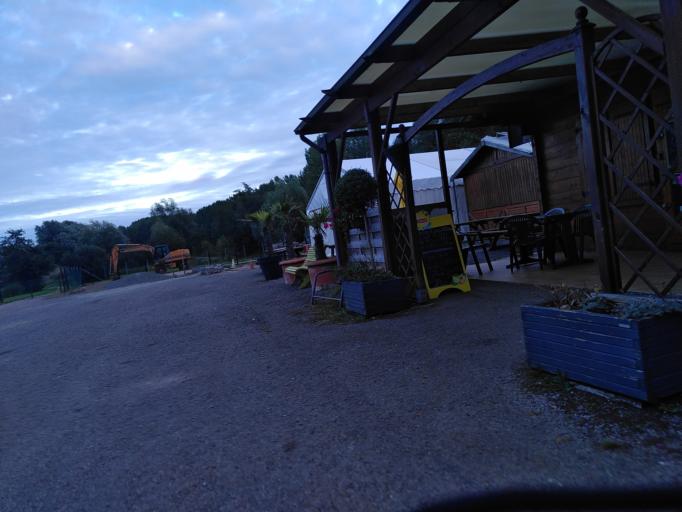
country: FR
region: Nord-Pas-de-Calais
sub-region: Departement du Pas-de-Calais
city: Mametz
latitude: 50.6393
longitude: 2.3015
